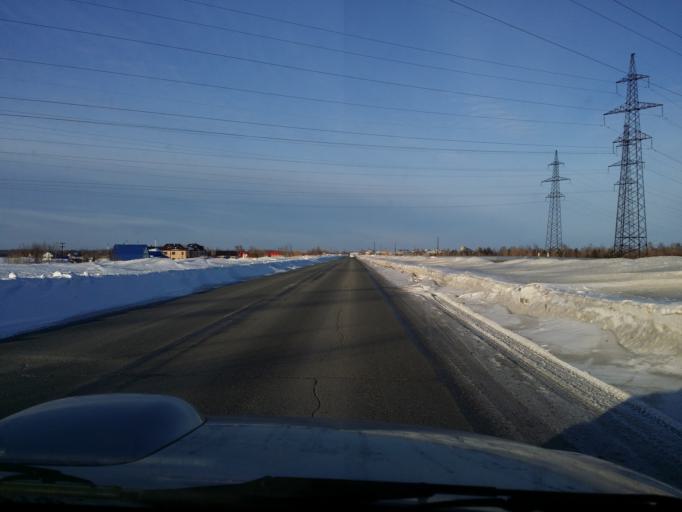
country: RU
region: Khanty-Mansiyskiy Avtonomnyy Okrug
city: Izluchinsk
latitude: 60.9688
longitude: 76.8883
